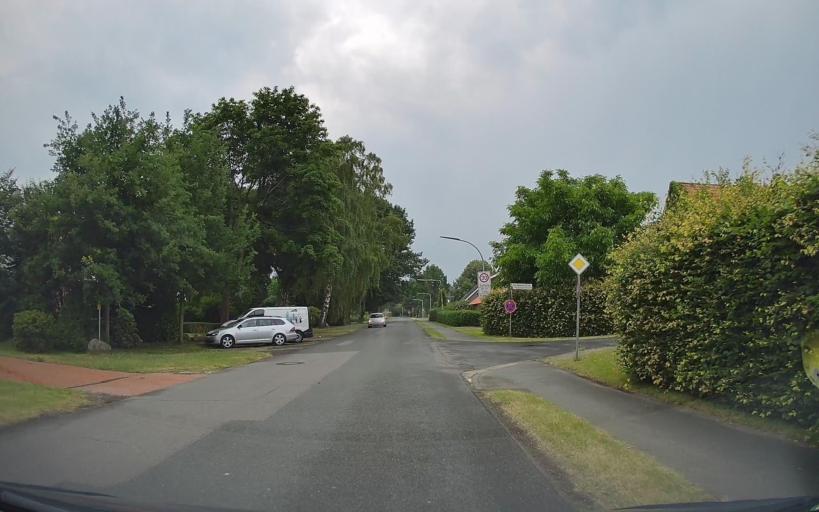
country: DE
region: Lower Saxony
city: Friesoythe
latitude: 53.0154
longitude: 7.8595
